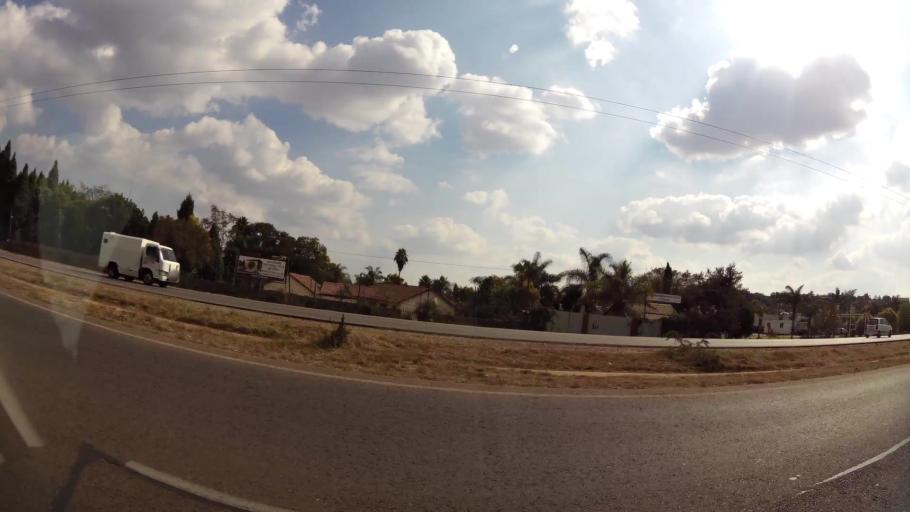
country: ZA
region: Gauteng
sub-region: City of Tshwane Metropolitan Municipality
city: Pretoria
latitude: -25.7909
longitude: 28.3268
